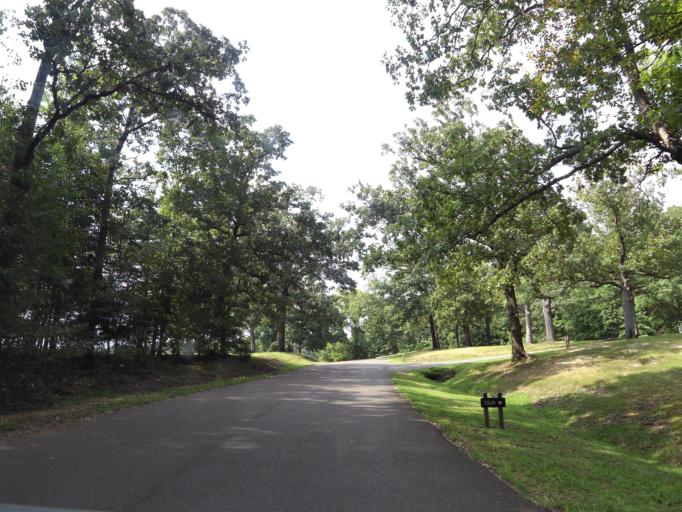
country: US
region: Tennessee
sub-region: Hardin County
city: Crump
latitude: 35.1296
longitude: -88.3298
